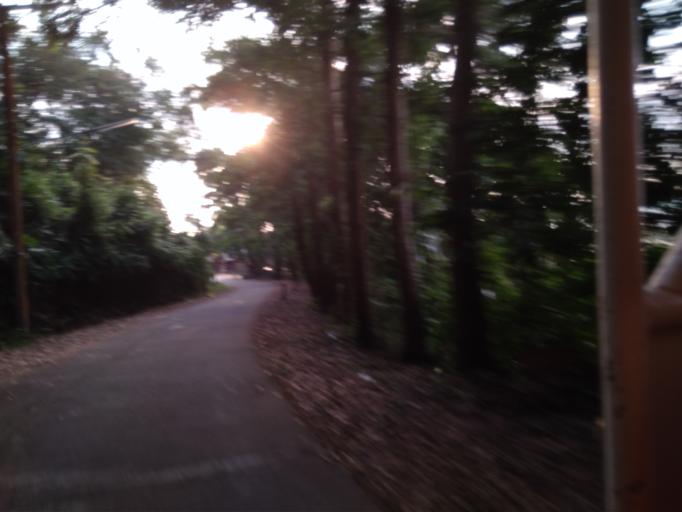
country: TH
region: Phangnga
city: Ko Yao
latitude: 8.1553
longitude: 98.6024
